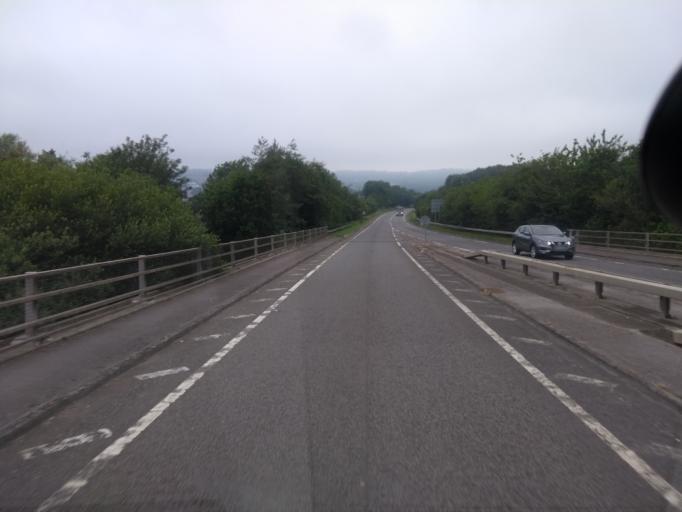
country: GB
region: England
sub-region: Dorset
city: Lyme Regis
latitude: 50.7404
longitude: -2.8895
